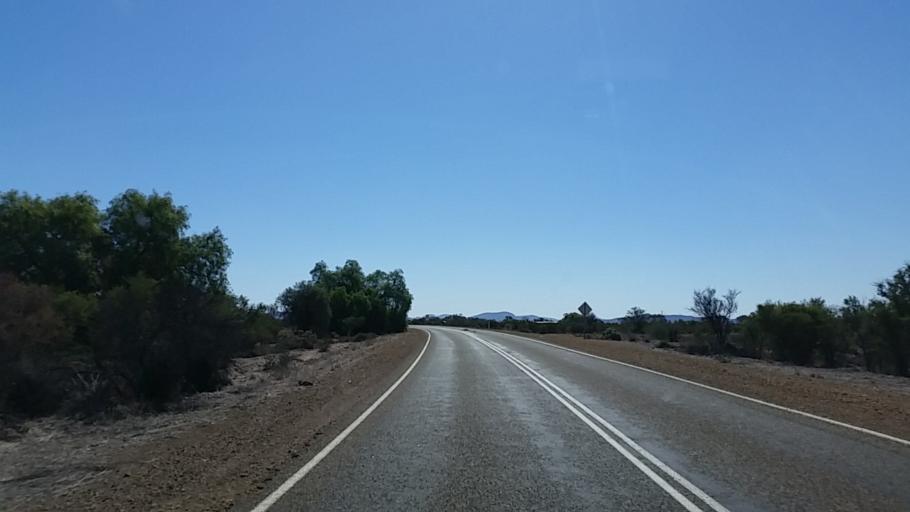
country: AU
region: South Australia
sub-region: Flinders Ranges
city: Quorn
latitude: -32.0762
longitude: 138.5010
